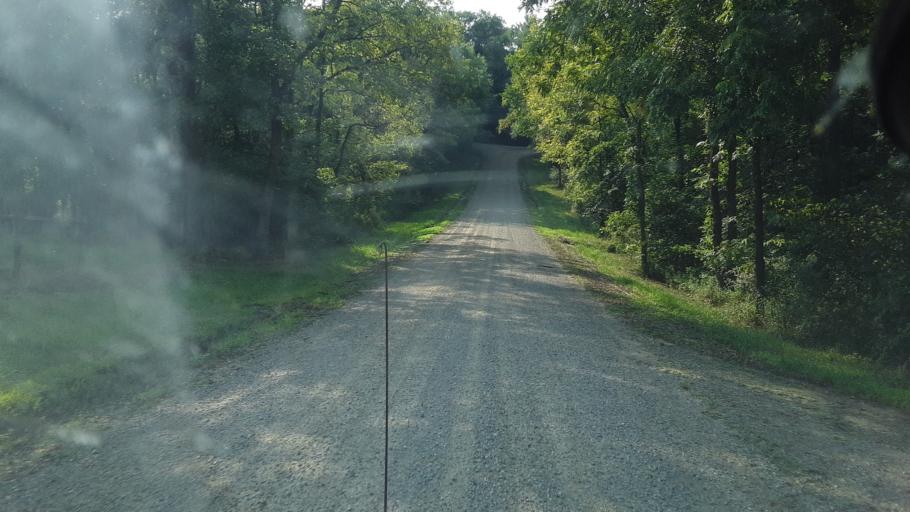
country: US
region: Ohio
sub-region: Knox County
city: Danville
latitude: 40.4229
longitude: -82.2895
